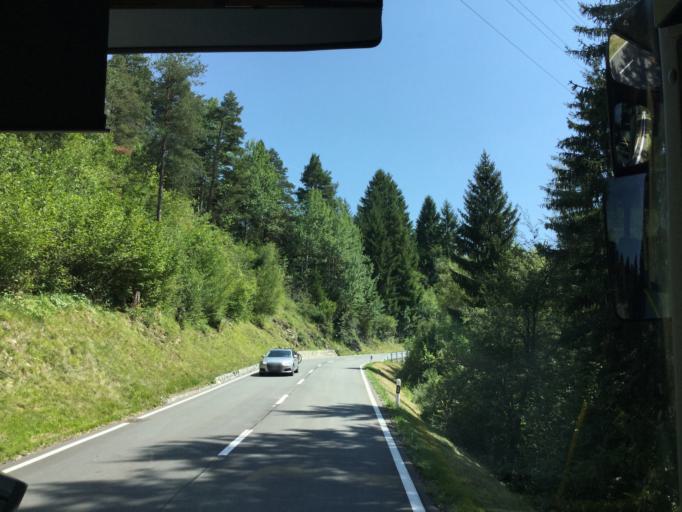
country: CH
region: Grisons
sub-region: Albula District
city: Tiefencastel
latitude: 46.6643
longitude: 9.5810
